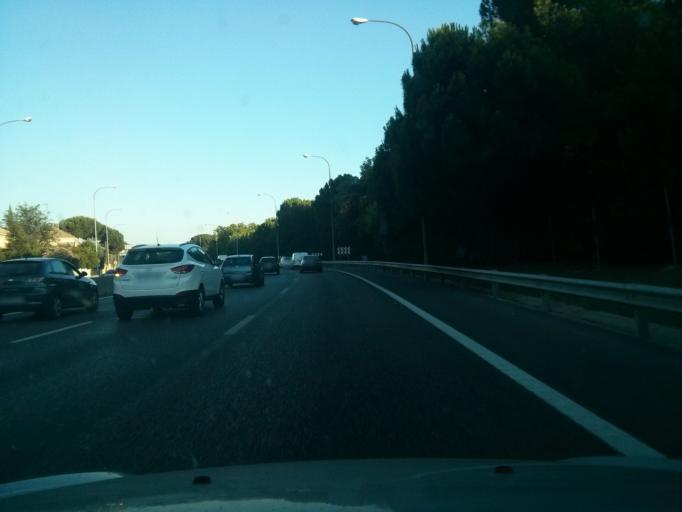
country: ES
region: Madrid
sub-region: Provincia de Madrid
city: Moncloa-Aravaca
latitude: 40.4307
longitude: -3.7373
